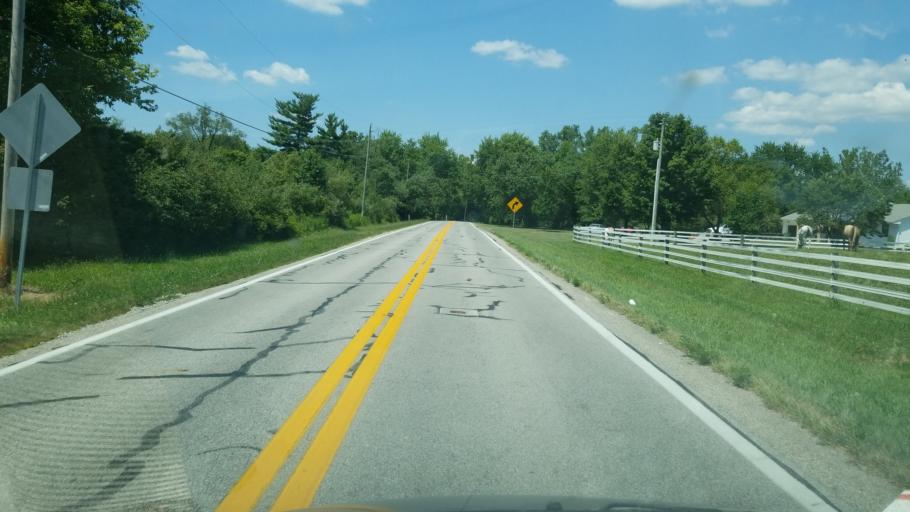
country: US
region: Ohio
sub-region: Franklin County
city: Lake Darby
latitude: 39.9928
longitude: -83.2455
